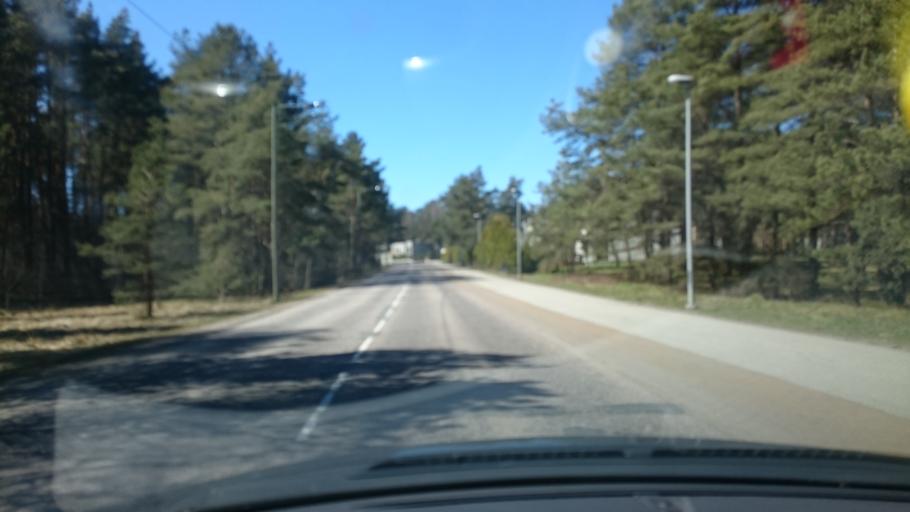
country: EE
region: Harju
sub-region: Tallinna linn
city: Kose
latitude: 59.4740
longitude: 24.8956
